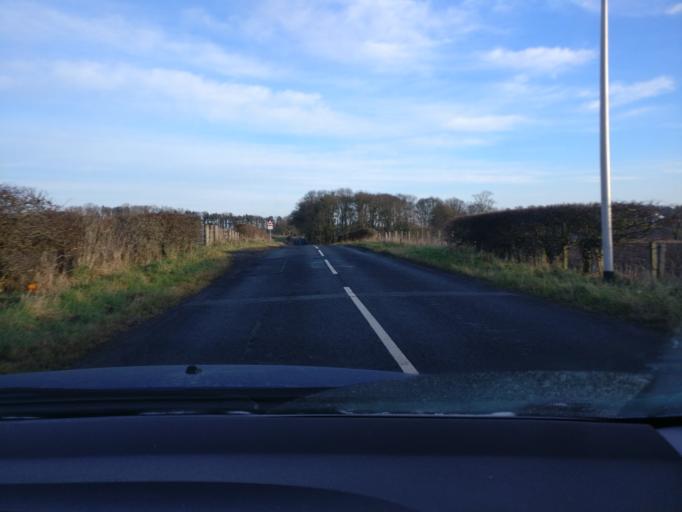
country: GB
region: Scotland
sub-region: The Scottish Borders
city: Hawick
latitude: 55.4401
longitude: -2.7724
